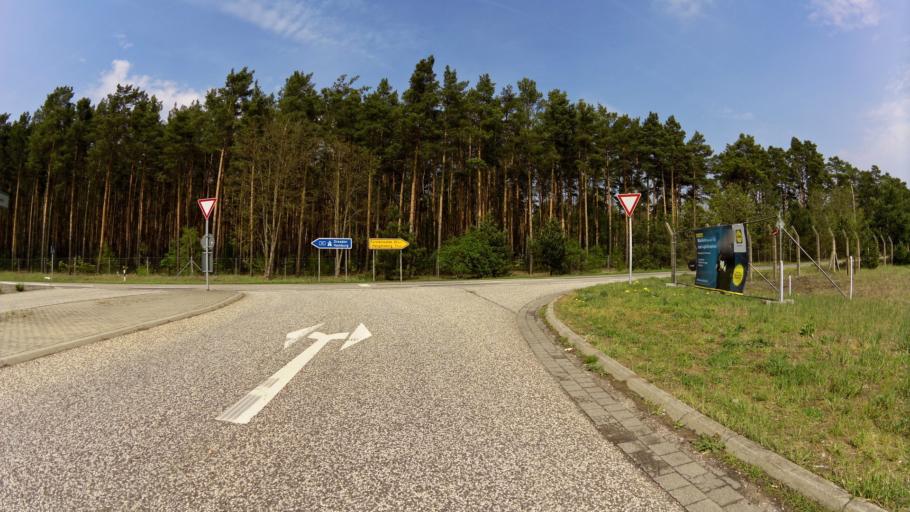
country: DE
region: Brandenburg
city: Grunheide
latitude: 52.3895
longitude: 13.7912
